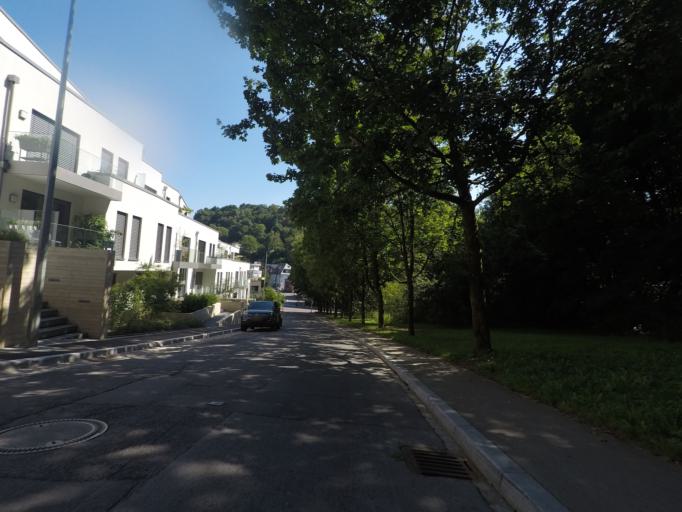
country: LU
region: Luxembourg
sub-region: Canton de Luxembourg
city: Luxembourg
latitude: 49.6292
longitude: 6.1126
